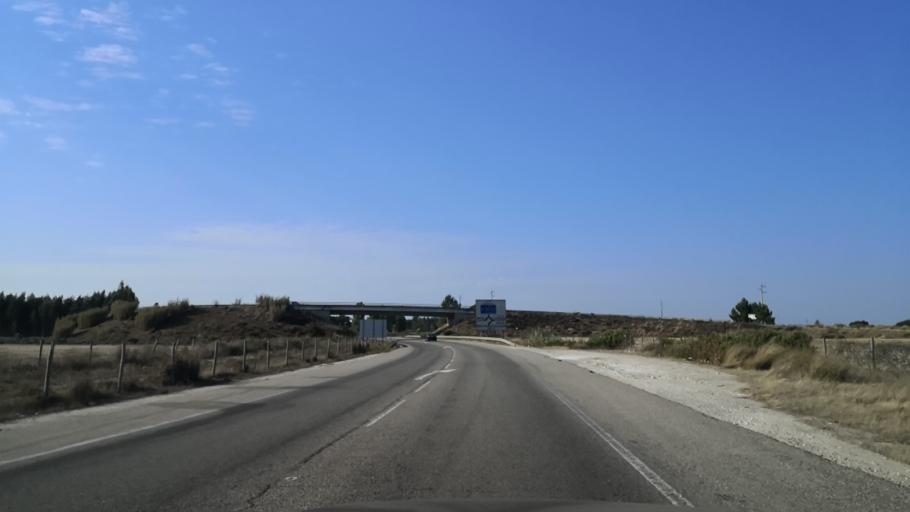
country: PT
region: Santarem
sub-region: Almeirim
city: Almeirim
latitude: 39.1709
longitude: -8.6206
